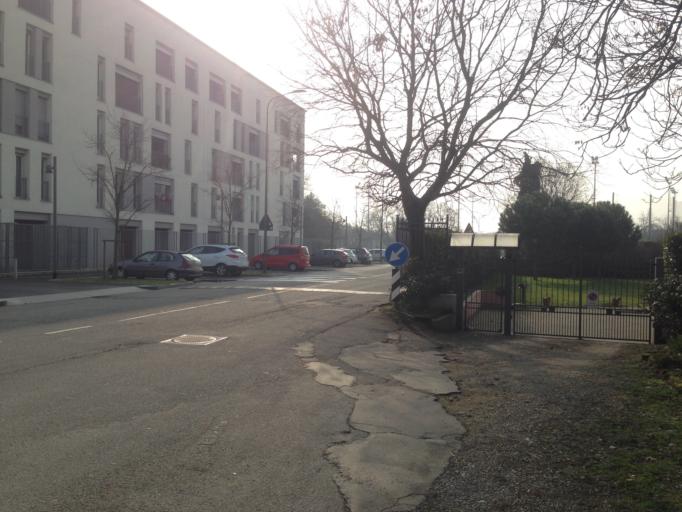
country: IT
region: Lombardy
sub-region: Citta metropolitana di Milano
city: Cesano Boscone
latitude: 45.4688
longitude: 9.1098
